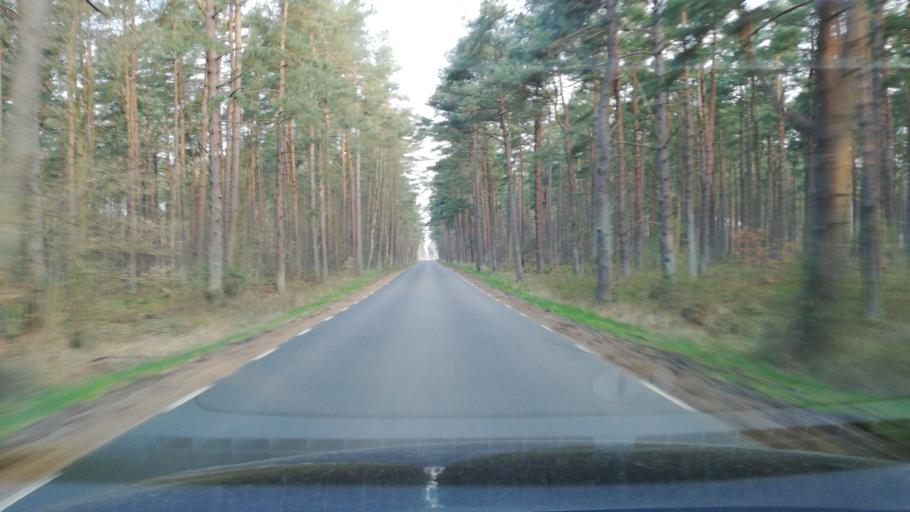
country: SE
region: Skane
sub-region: Simrishamns Kommun
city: Simrishamn
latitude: 55.3914
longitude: 14.1858
